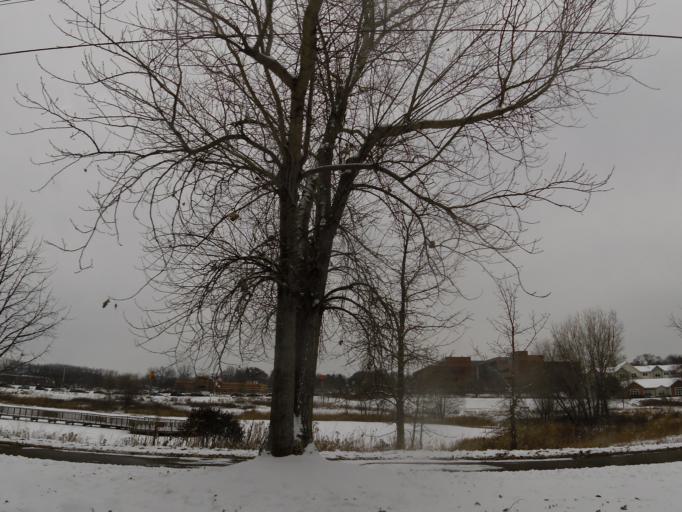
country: US
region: Minnesota
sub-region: Ramsey County
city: Maplewood
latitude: 44.9739
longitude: -93.0404
